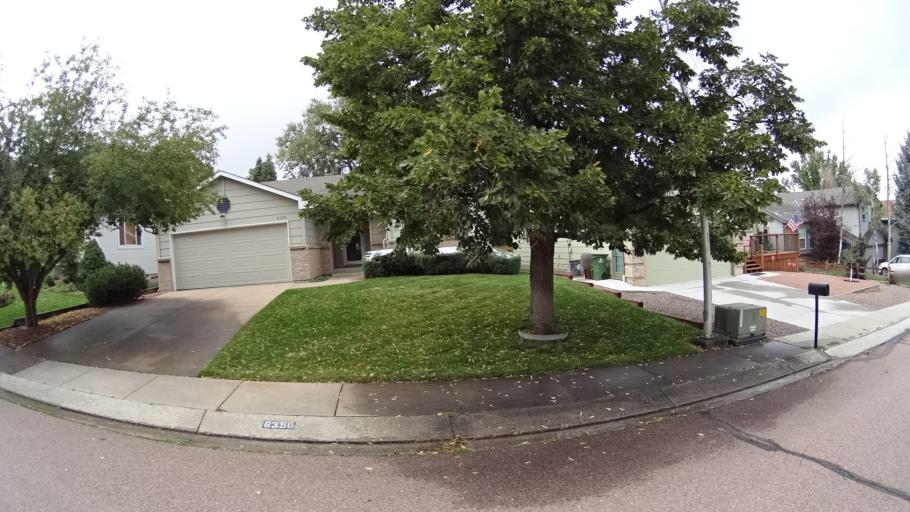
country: US
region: Colorado
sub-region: El Paso County
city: Cimarron Hills
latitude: 38.9240
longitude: -104.7647
